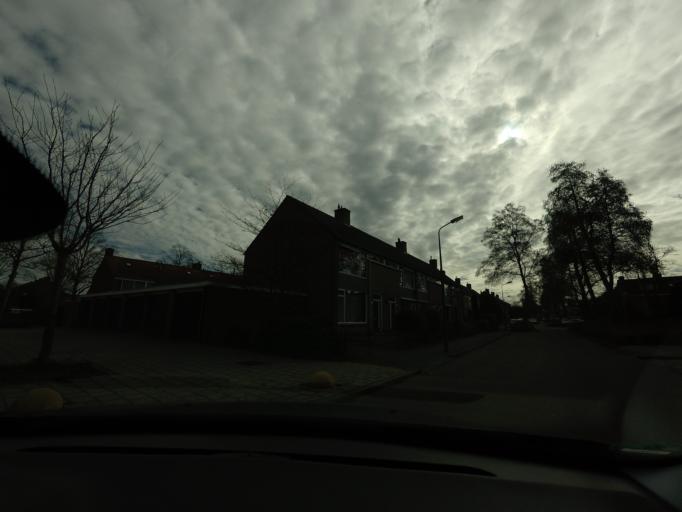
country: NL
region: Utrecht
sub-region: Gemeente Woerden
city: Woerden
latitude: 52.0825
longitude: 4.8708
